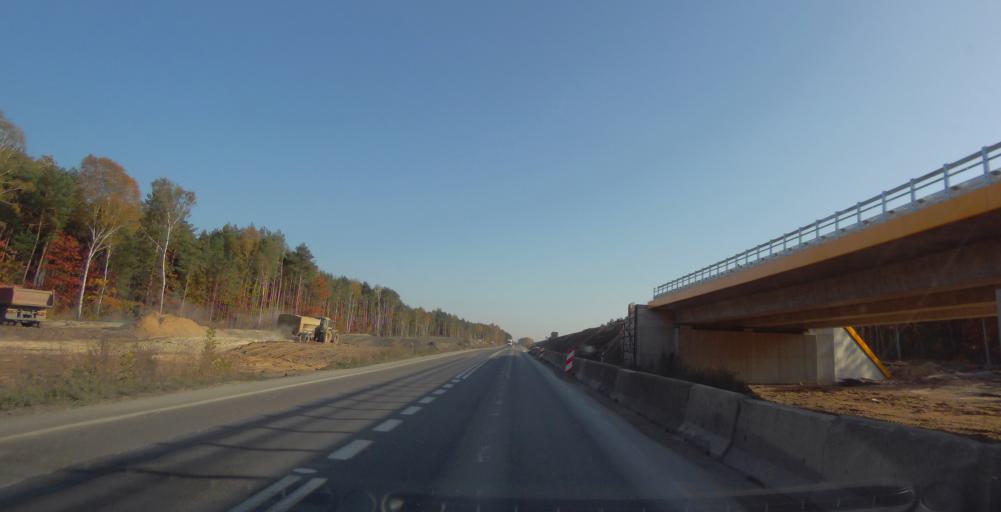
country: PL
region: Masovian Voivodeship
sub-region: Powiat otwocki
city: Celestynow
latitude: 52.0849
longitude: 21.4310
